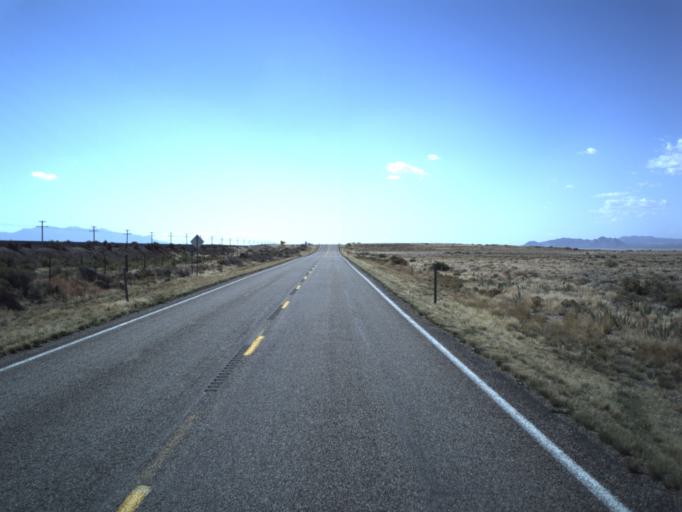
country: US
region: Utah
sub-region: Beaver County
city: Milford
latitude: 38.6700
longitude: -112.9807
